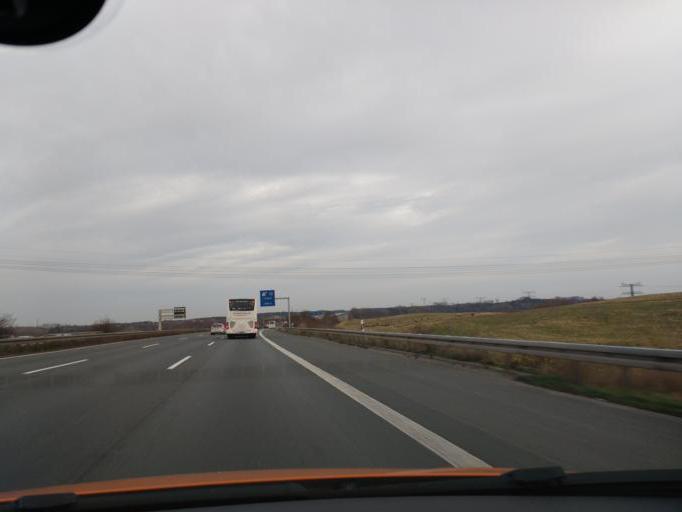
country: DE
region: Saxony-Anhalt
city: Glindenberg
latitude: 52.2183
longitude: 11.6800
